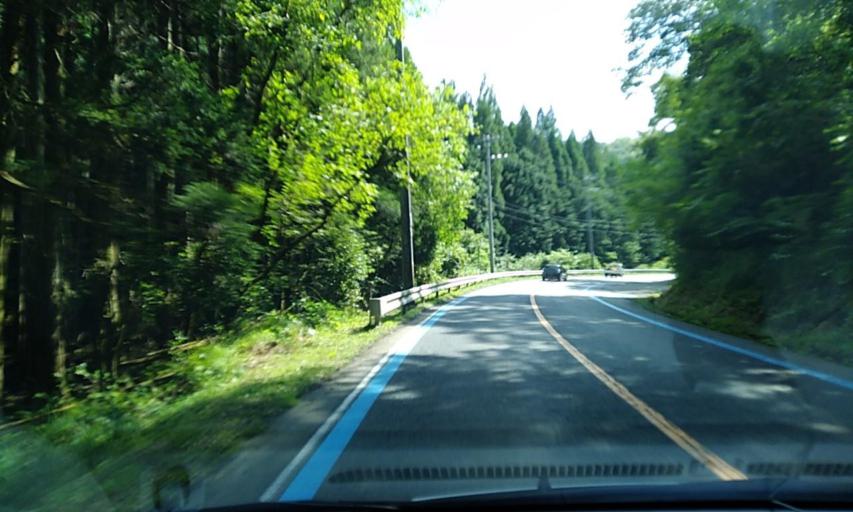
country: JP
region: Kyoto
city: Ayabe
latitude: 35.3051
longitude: 135.2973
